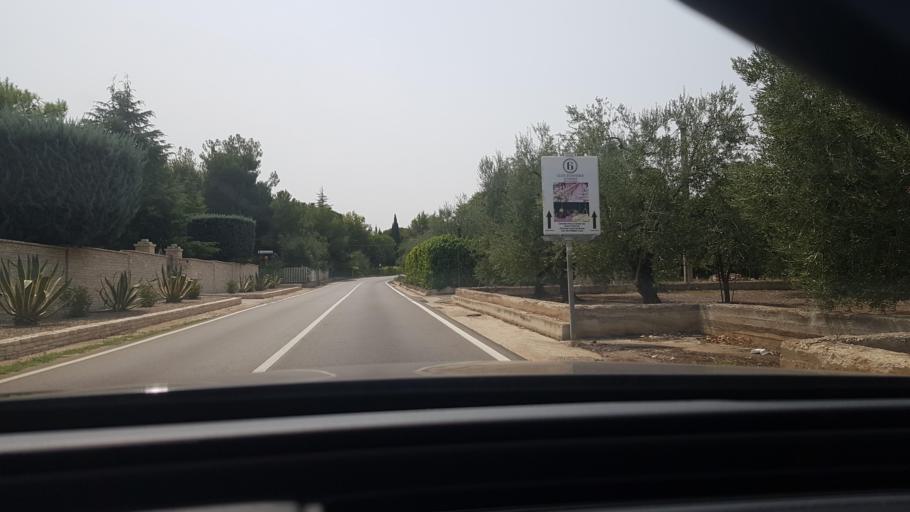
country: IT
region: Apulia
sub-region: Provincia di Barletta - Andria - Trani
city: Andria
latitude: 41.1478
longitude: 16.2906
